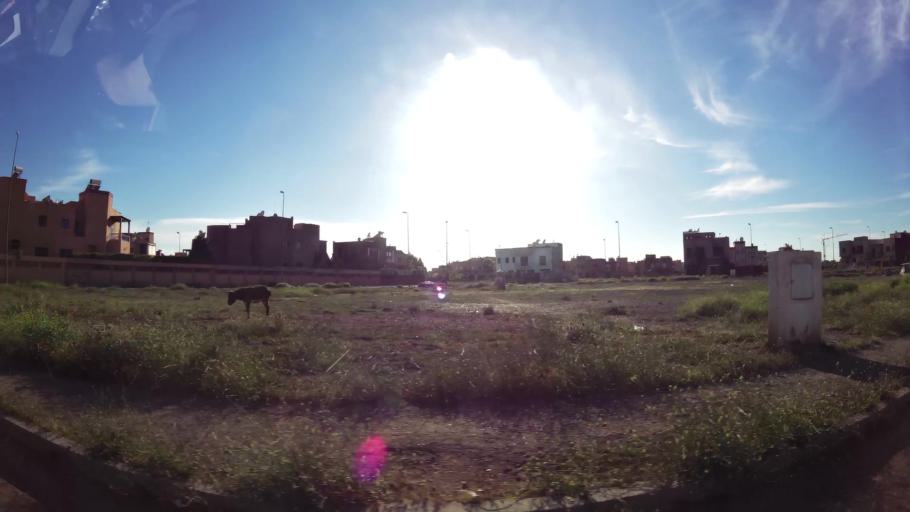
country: MA
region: Marrakech-Tensift-Al Haouz
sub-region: Marrakech
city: Marrakesh
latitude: 31.6764
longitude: -8.0591
